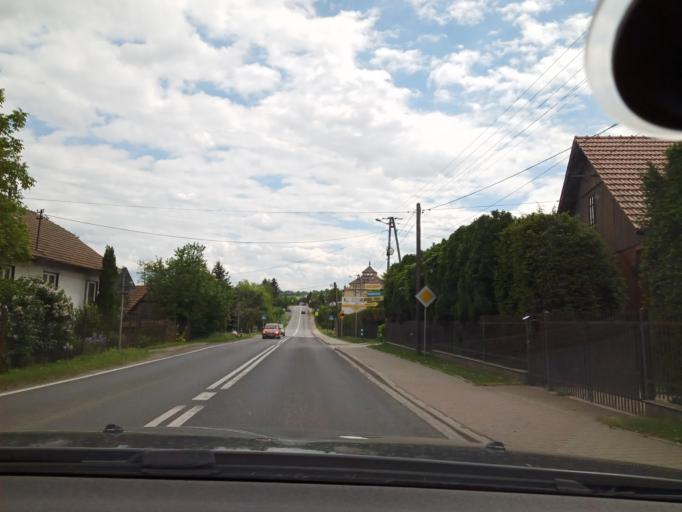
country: PL
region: Lesser Poland Voivodeship
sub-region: Powiat wielicki
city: Trabki
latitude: 49.9610
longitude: 20.1431
